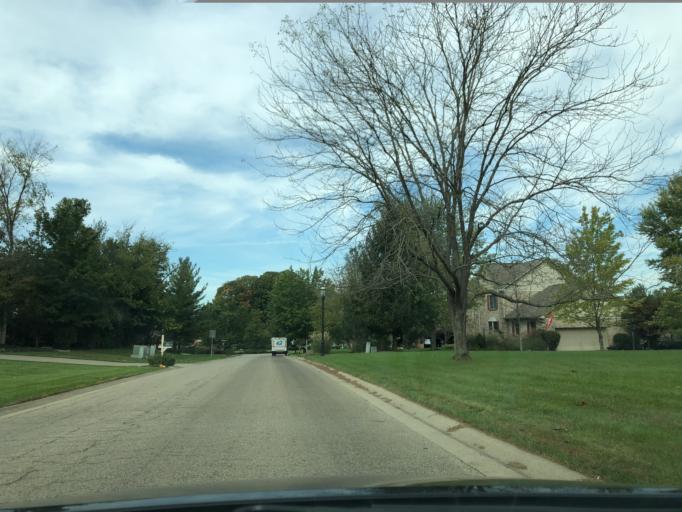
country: US
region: Ohio
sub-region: Hamilton County
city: Loveland
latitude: 39.2452
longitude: -84.2681
